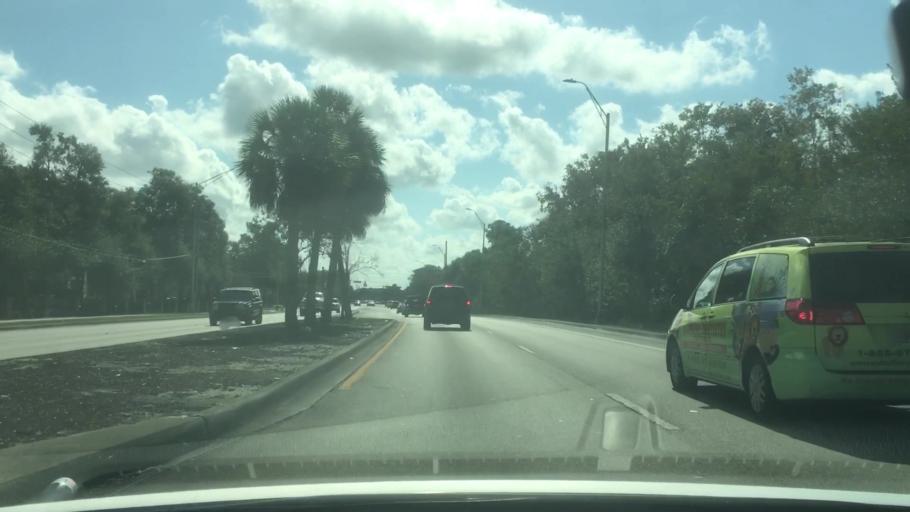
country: US
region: Florida
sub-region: Duval County
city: Jacksonville
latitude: 30.3329
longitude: -81.5470
